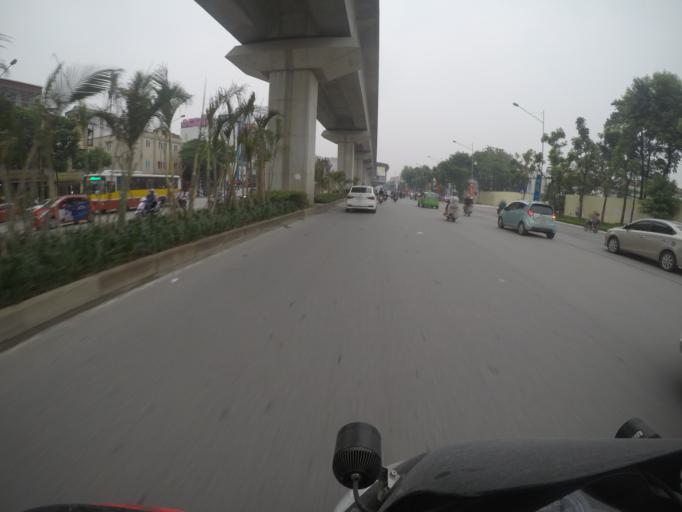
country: VN
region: Ha Noi
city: Thanh Xuan
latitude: 20.9963
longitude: 105.8102
